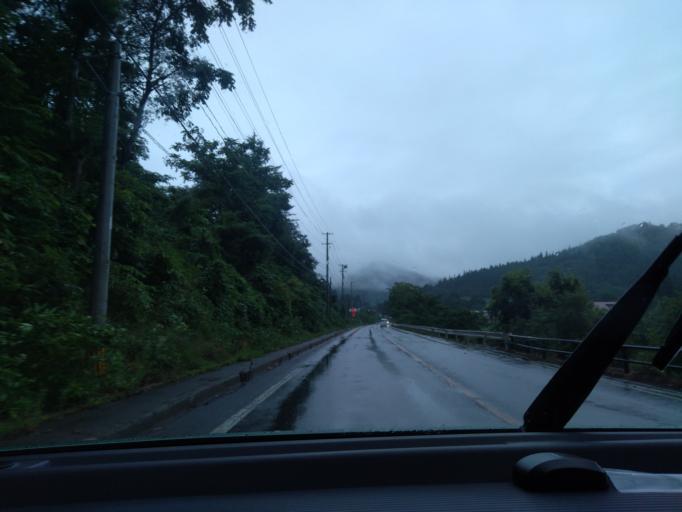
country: JP
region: Akita
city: Yokotemachi
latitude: 39.2958
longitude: 140.6283
